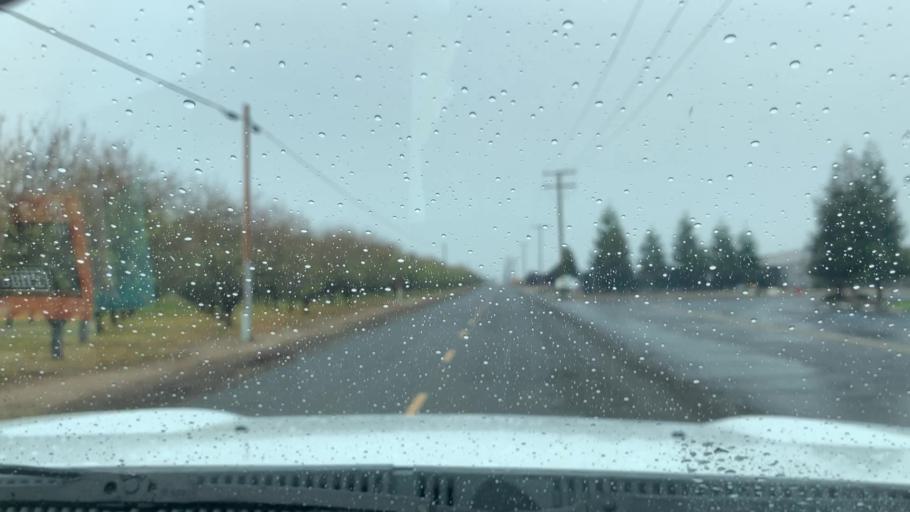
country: US
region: California
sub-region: Tulare County
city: Earlimart
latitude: 35.8339
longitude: -119.2554
